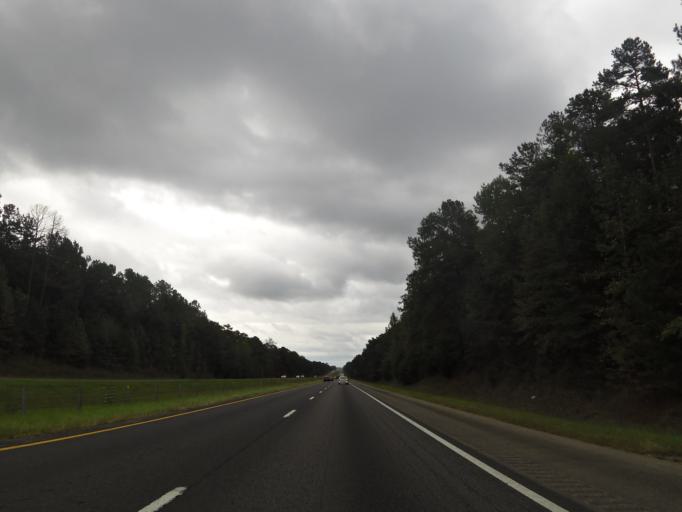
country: US
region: Alabama
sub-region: Butler County
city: Georgiana
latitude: 31.6088
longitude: -86.8176
